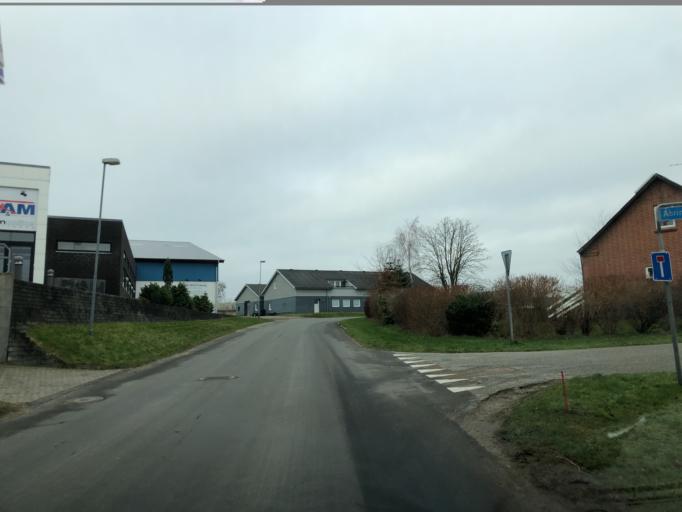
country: DK
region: Central Jutland
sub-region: Viborg Kommune
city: Stoholm
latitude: 56.4863
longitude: 9.1566
